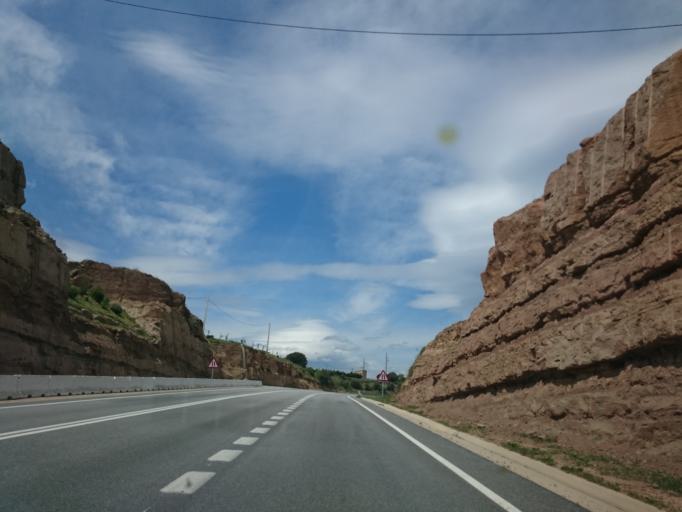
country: ES
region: Catalonia
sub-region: Provincia de Barcelona
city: Prats de Llucanes
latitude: 42.0143
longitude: 2.0349
